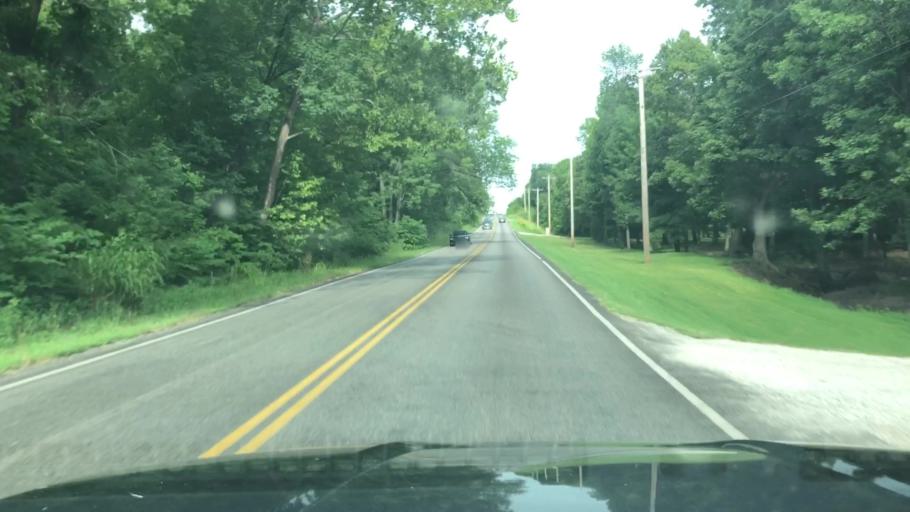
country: US
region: Oklahoma
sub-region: Tulsa County
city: Oakhurst
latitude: 36.0901
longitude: -96.1065
